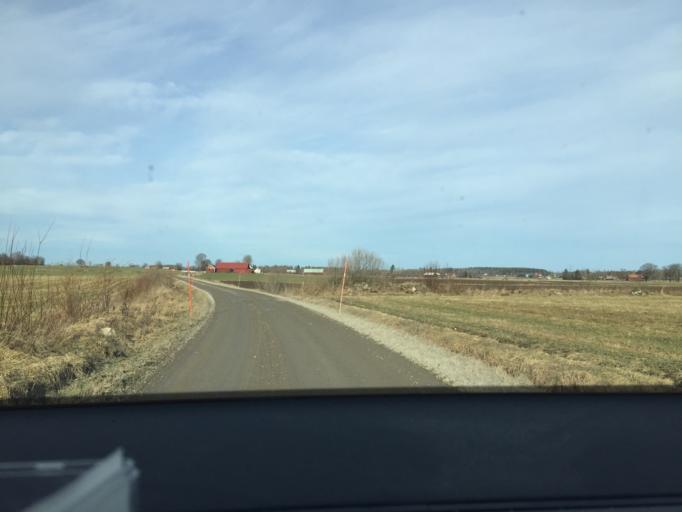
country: SE
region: OErebro
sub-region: Hallsbergs Kommun
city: Skollersta
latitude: 59.1271
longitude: 15.4316
